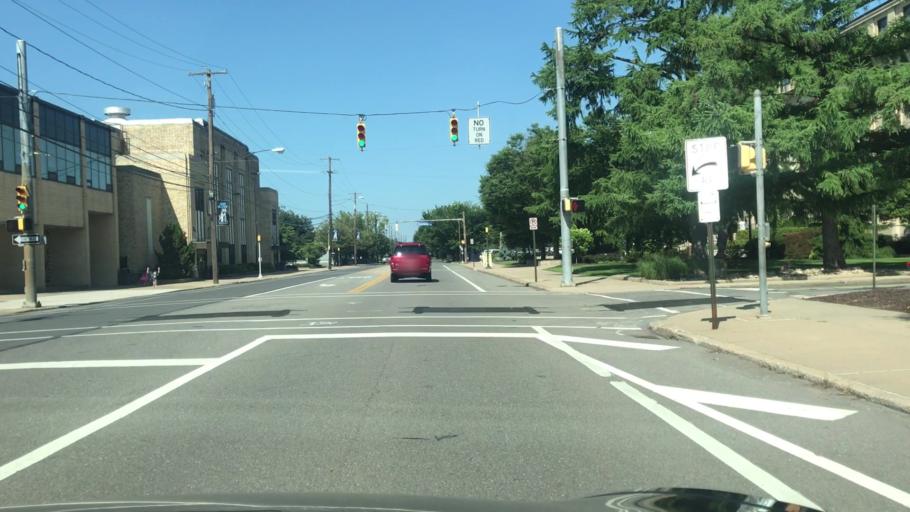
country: US
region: Pennsylvania
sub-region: Lycoming County
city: Duboistown
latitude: 41.2375
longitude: -77.0248
